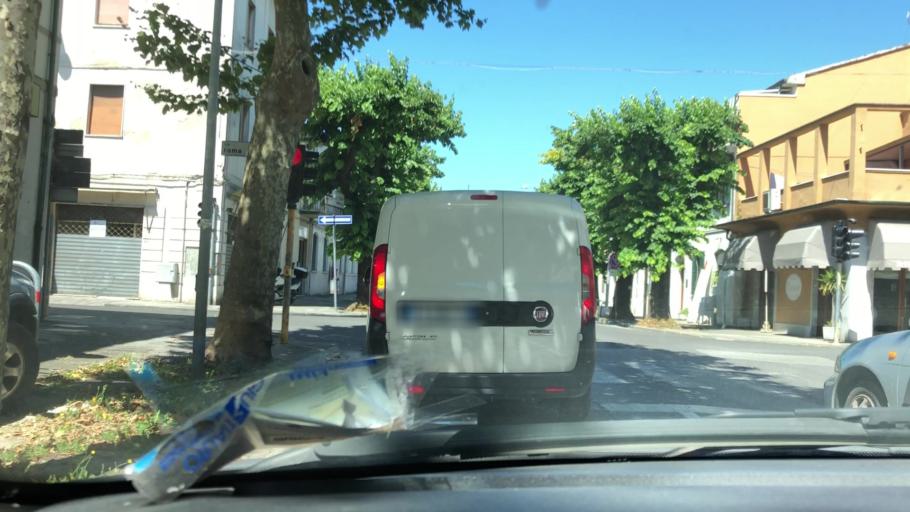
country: IT
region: Tuscany
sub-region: Province of Pisa
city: Pontedera
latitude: 43.6608
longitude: 10.6342
